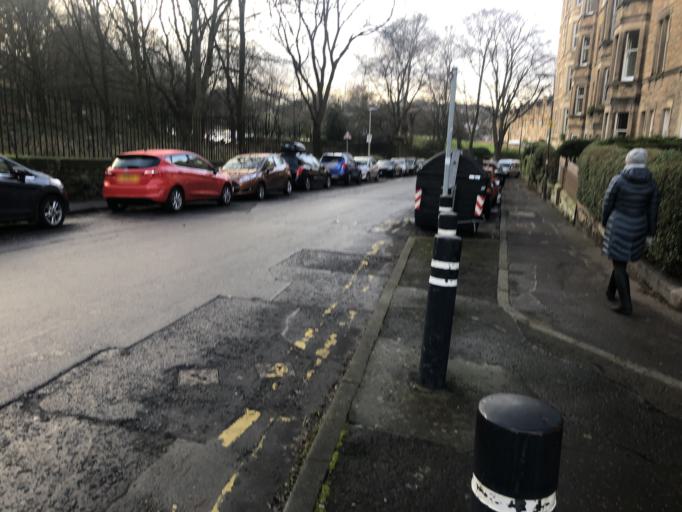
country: GB
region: Scotland
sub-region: West Lothian
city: Seafield
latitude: 55.9544
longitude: -3.1561
